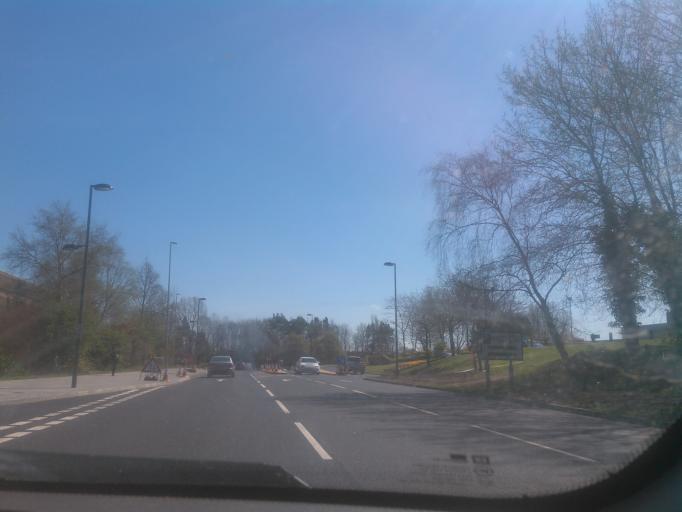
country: GB
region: England
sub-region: Telford and Wrekin
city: Telford
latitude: 52.6783
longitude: -2.4441
